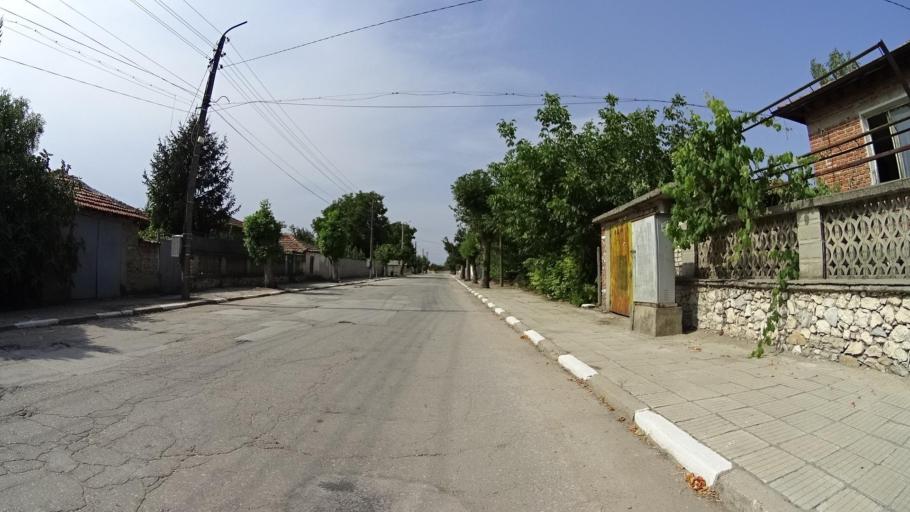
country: BG
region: Plovdiv
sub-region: Obshtina Kaloyanovo
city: Kaloyanovo
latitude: 42.2648
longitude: 24.8005
